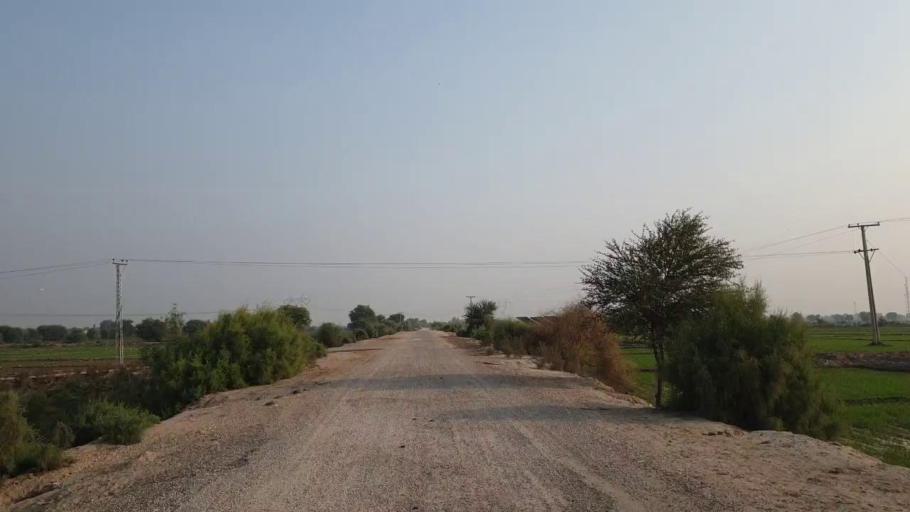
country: PK
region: Sindh
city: Bhan
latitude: 26.4970
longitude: 67.7677
